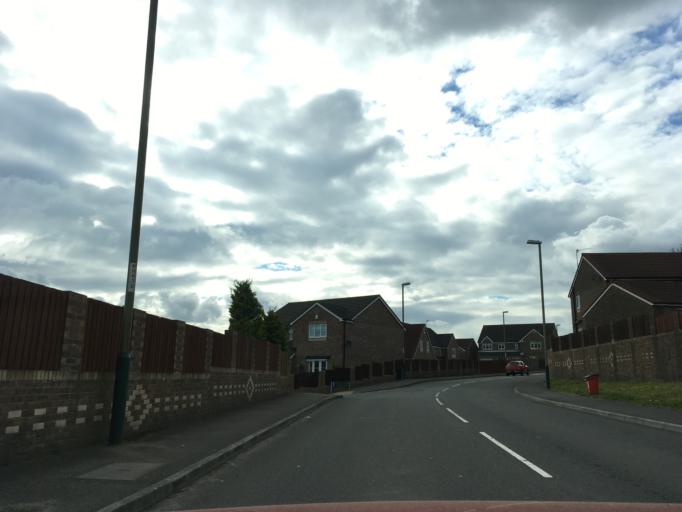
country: GB
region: Wales
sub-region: Caerphilly County Borough
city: Nelson
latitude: 51.6488
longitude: -3.2867
